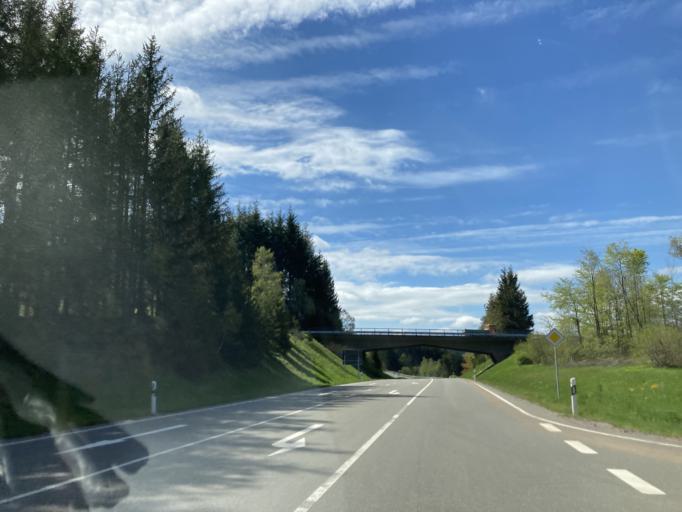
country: DE
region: Baden-Wuerttemberg
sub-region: Freiburg Region
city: Gutenbach
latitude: 48.0270
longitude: 8.1787
